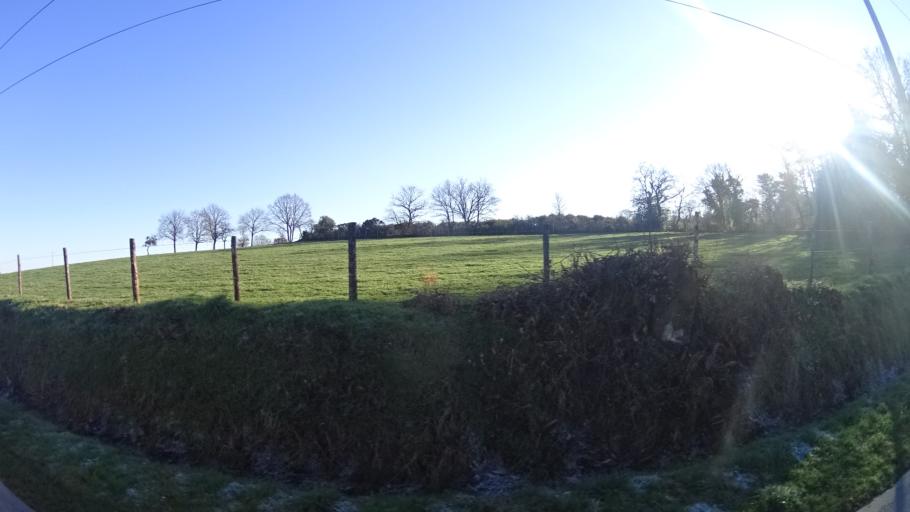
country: FR
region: Brittany
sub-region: Departement du Morbihan
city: Saint-Jacut-les-Pins
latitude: 47.6598
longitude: -2.2040
